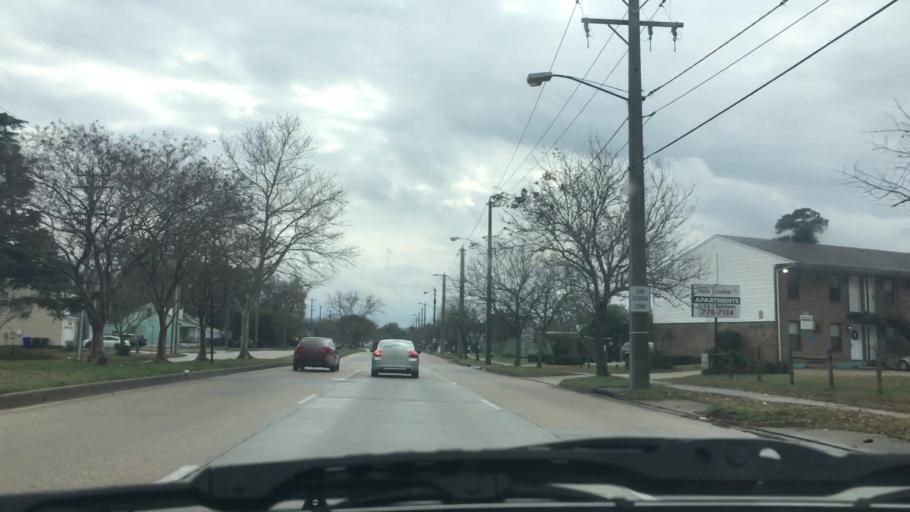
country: US
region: Virginia
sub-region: City of Norfolk
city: Norfolk
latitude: 36.8959
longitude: -76.2386
